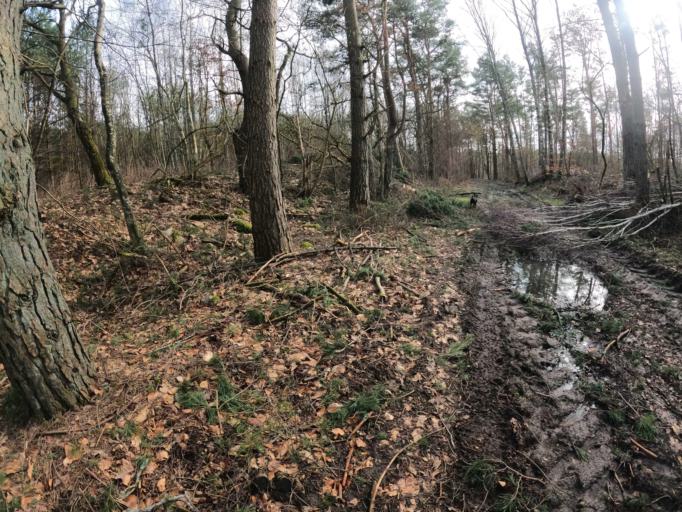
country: PL
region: West Pomeranian Voivodeship
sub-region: Powiat koszalinski
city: Bobolice
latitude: 53.9733
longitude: 16.5792
